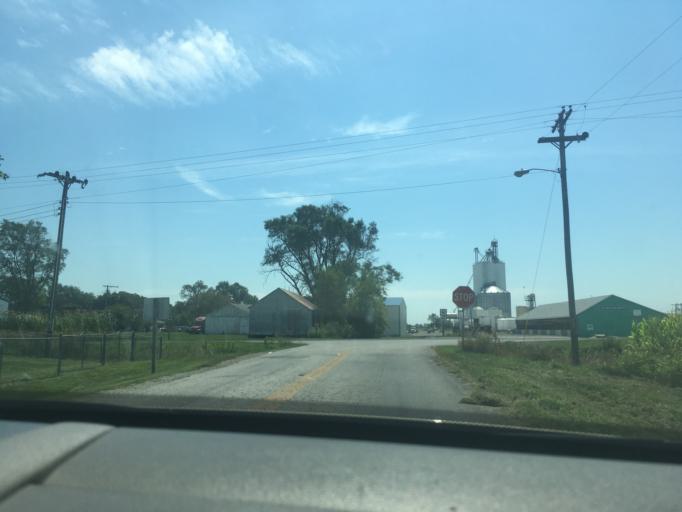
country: US
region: Missouri
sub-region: Gentry County
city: Stanberry
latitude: 40.1708
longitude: -94.7383
